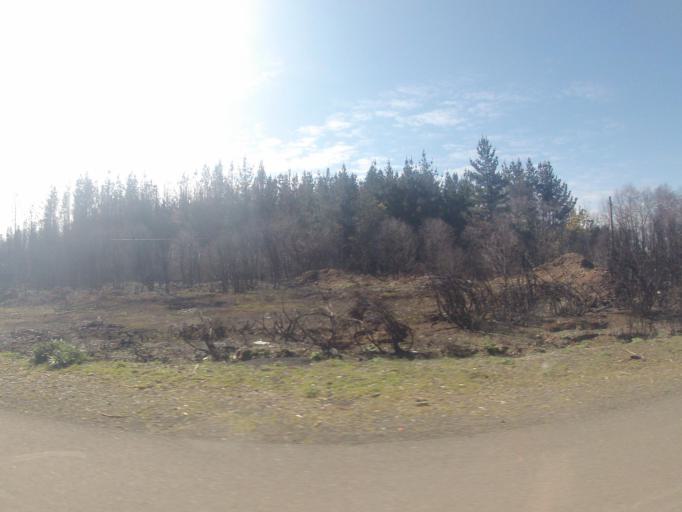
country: CL
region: Araucania
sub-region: Provincia de Malleco
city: Victoria
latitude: -38.1506
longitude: -72.3063
